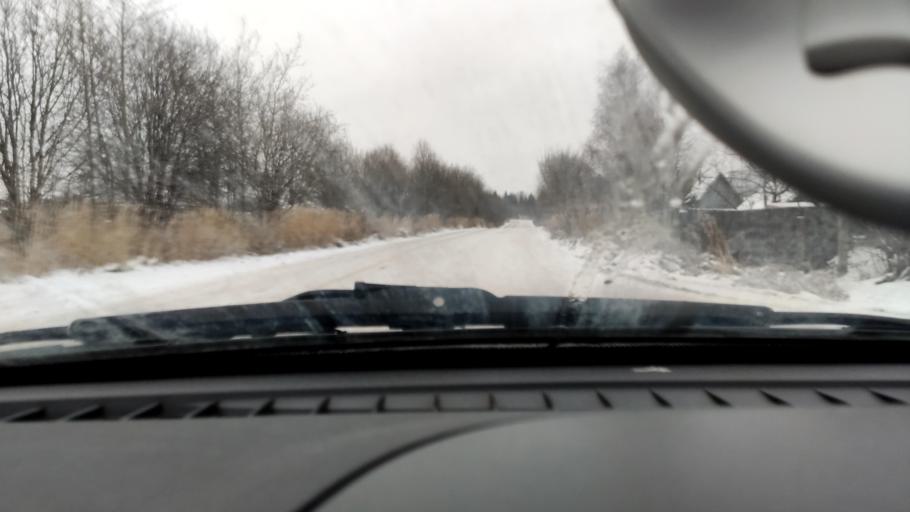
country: RU
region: Perm
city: Polazna
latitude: 58.1768
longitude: 56.4068
